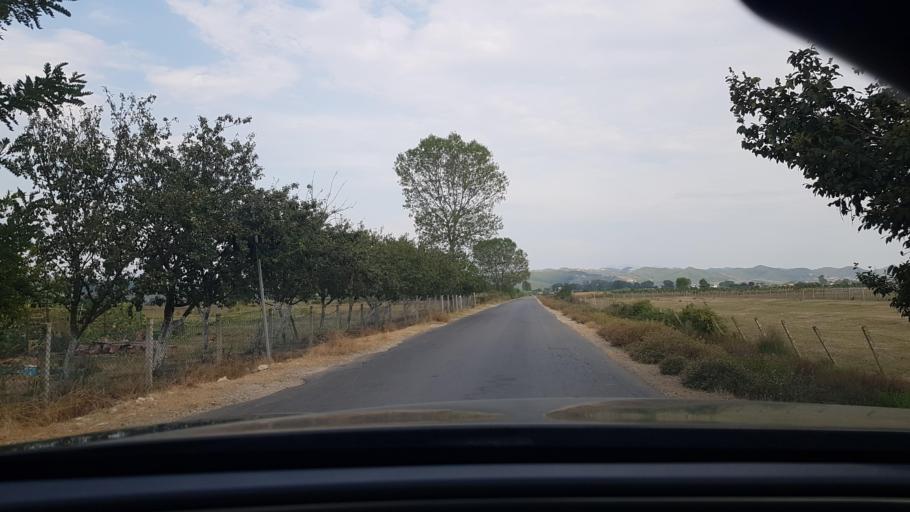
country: AL
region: Durres
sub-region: Rrethi i Durresit
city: Katundi i Ri
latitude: 41.4845
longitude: 19.5290
